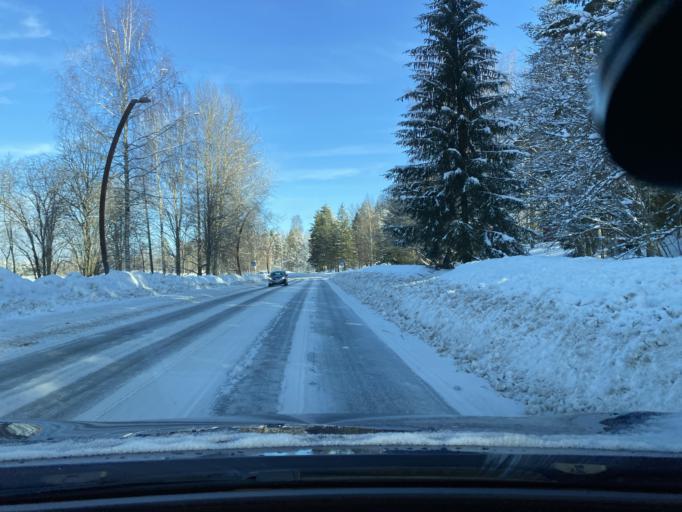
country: FI
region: Southern Savonia
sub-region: Mikkeli
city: Kangasniemi
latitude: 61.9928
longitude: 26.6455
